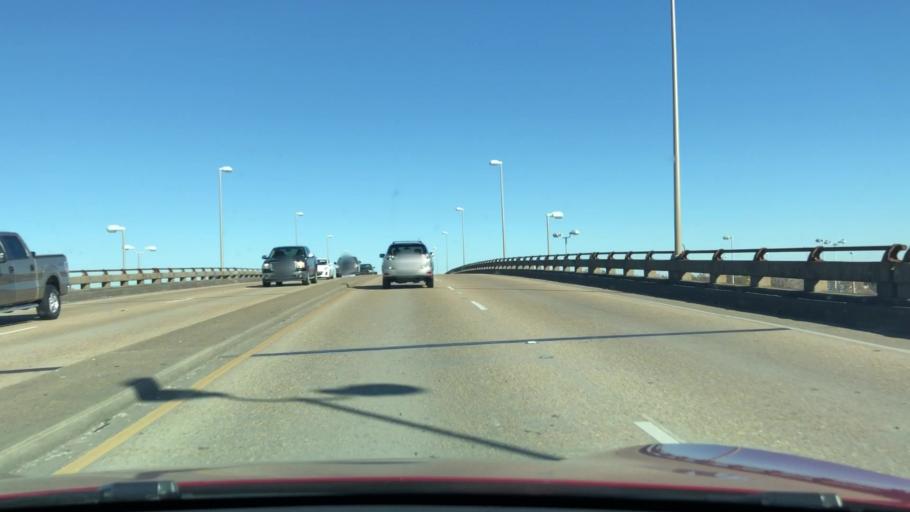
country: US
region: Louisiana
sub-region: Jefferson Parish
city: Jefferson
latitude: 29.9736
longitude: -90.1564
